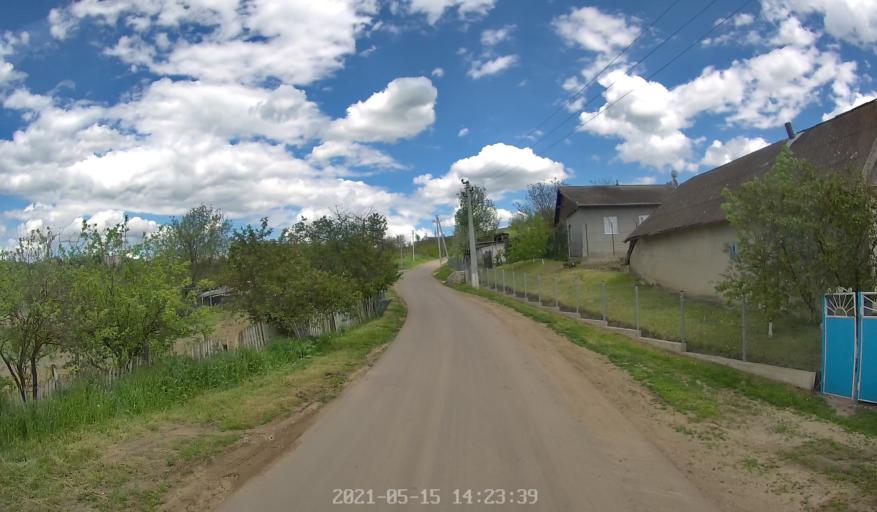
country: MD
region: Hincesti
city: Hincesti
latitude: 46.7387
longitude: 28.5171
